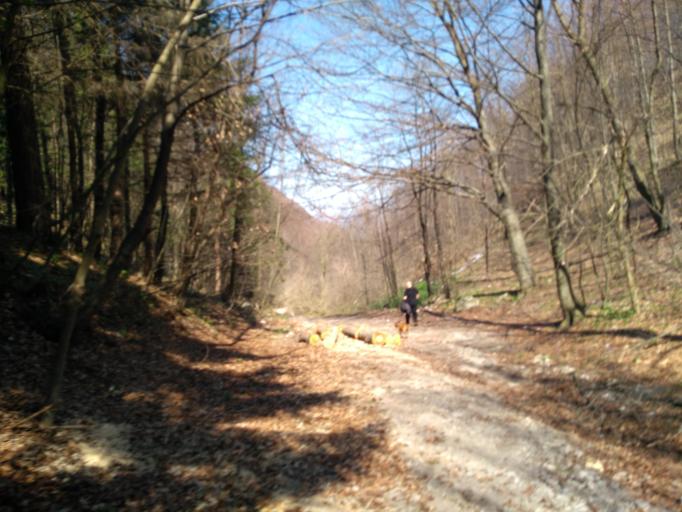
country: HR
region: Varazdinska
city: Ivanec
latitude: 46.1885
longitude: 16.1156
